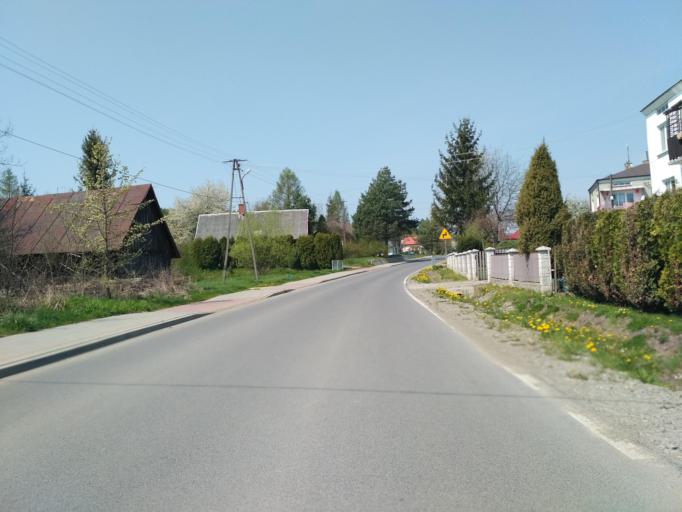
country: PL
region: Subcarpathian Voivodeship
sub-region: Powiat krosnienski
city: Chorkowka
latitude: 49.6518
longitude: 21.6726
